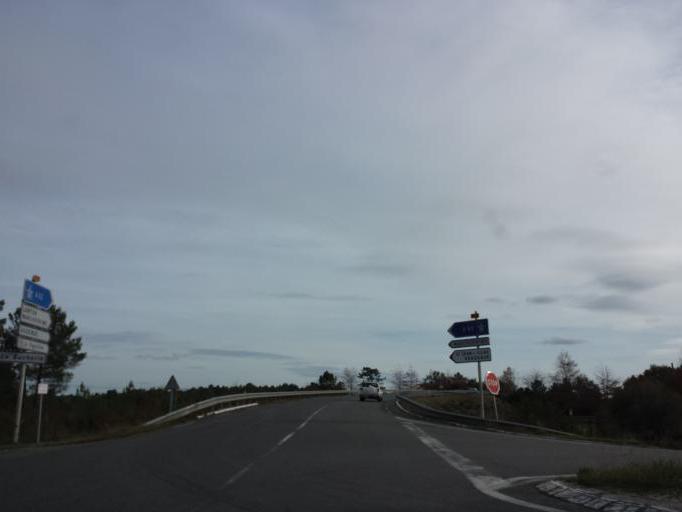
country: FR
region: Aquitaine
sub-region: Departement de la Gironde
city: Marcheprime
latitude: 44.7844
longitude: -0.9338
